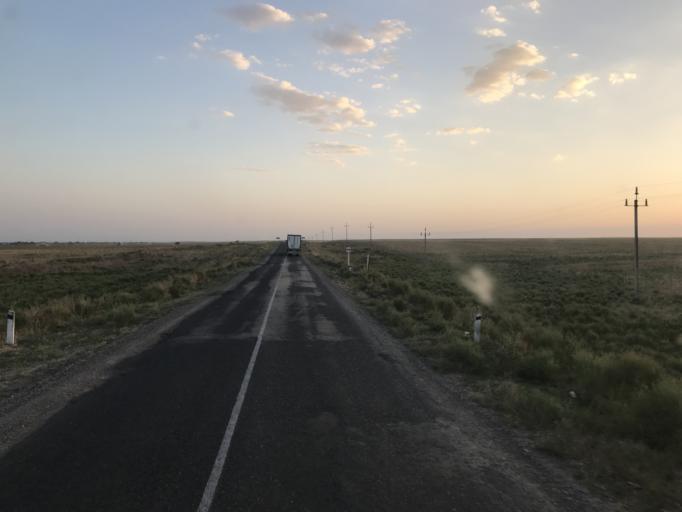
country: UZ
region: Toshkent
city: Yangiyul
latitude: 41.3652
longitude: 68.7353
